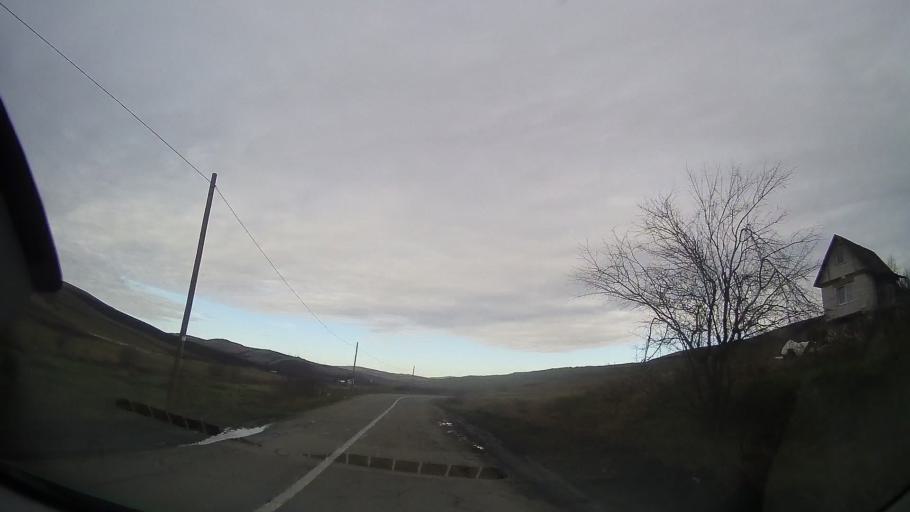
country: RO
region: Cluj
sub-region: Comuna Camarasu
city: Camarasu
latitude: 46.8083
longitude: 24.1439
